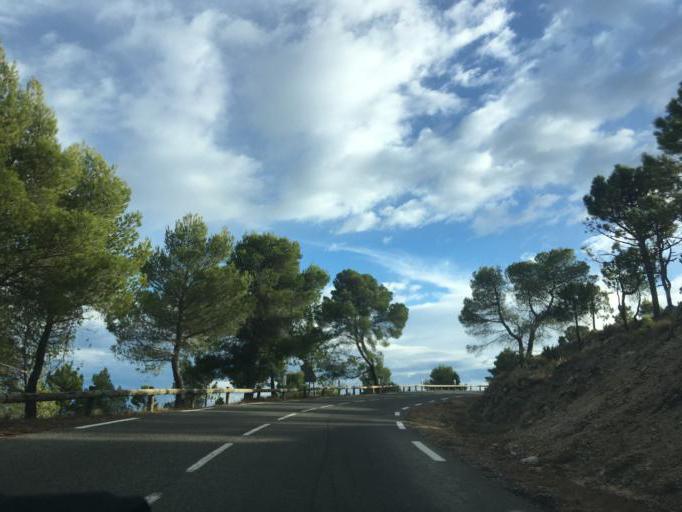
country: FR
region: Provence-Alpes-Cote d'Azur
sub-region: Departement du Var
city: Villecroze
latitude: 43.5864
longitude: 6.2647
